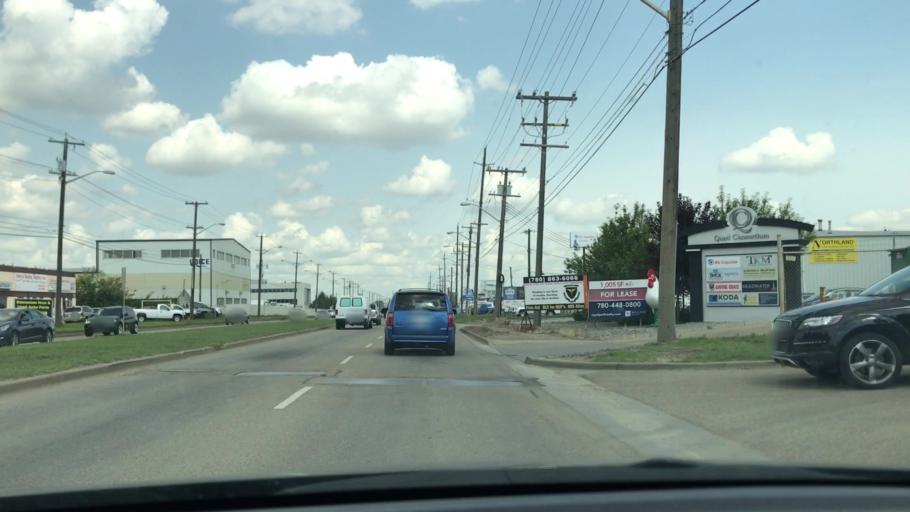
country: CA
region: Alberta
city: Edmonton
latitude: 53.5089
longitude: -113.4182
